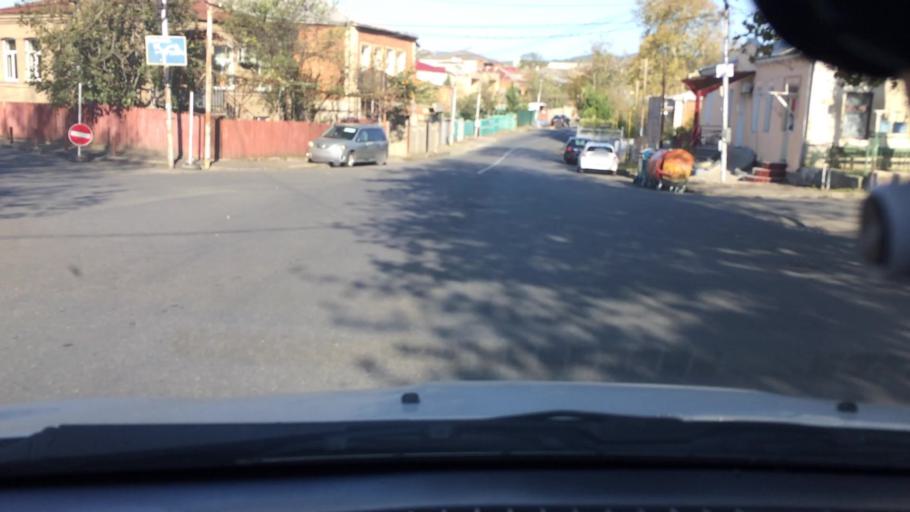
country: GE
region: Imereti
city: Kutaisi
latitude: 42.2691
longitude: 42.7149
